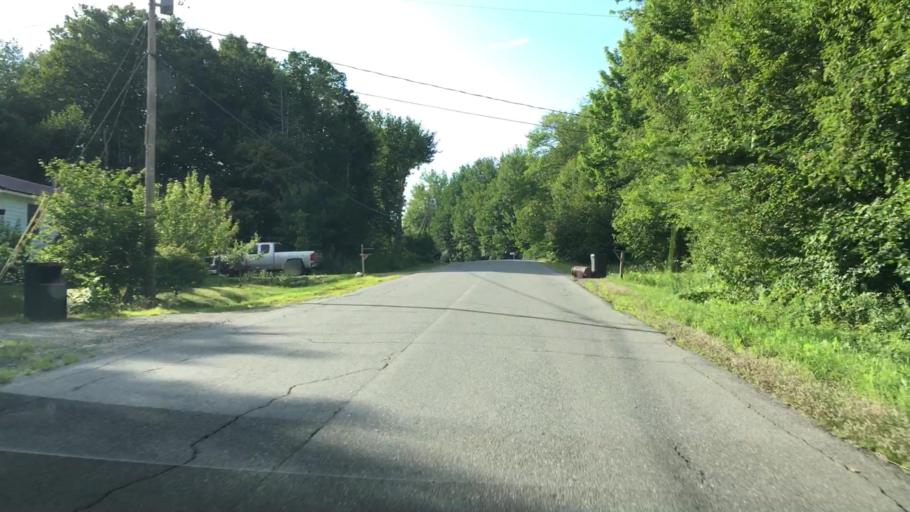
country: US
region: Maine
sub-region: Waldo County
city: Stockton Springs
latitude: 44.4915
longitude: -68.8683
